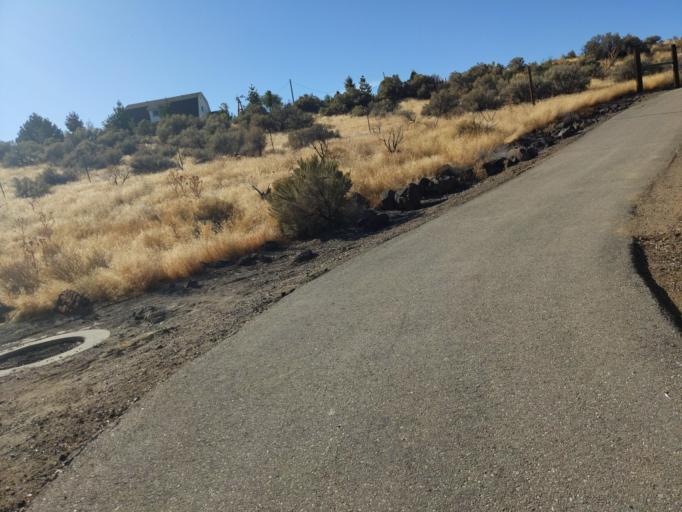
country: US
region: Idaho
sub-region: Elmore County
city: Mountain Home
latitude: 43.1451
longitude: -115.6723
